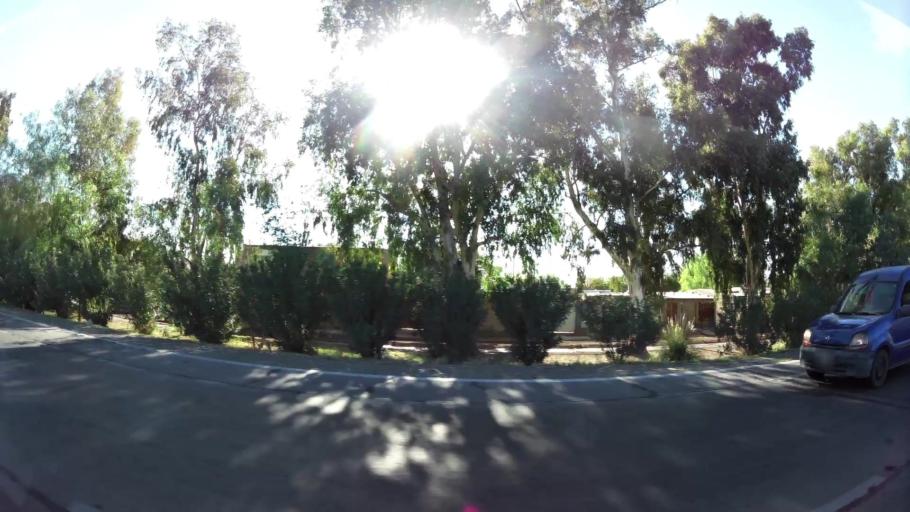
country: AR
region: Mendoza
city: Las Heras
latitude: -32.8345
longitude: -68.8066
